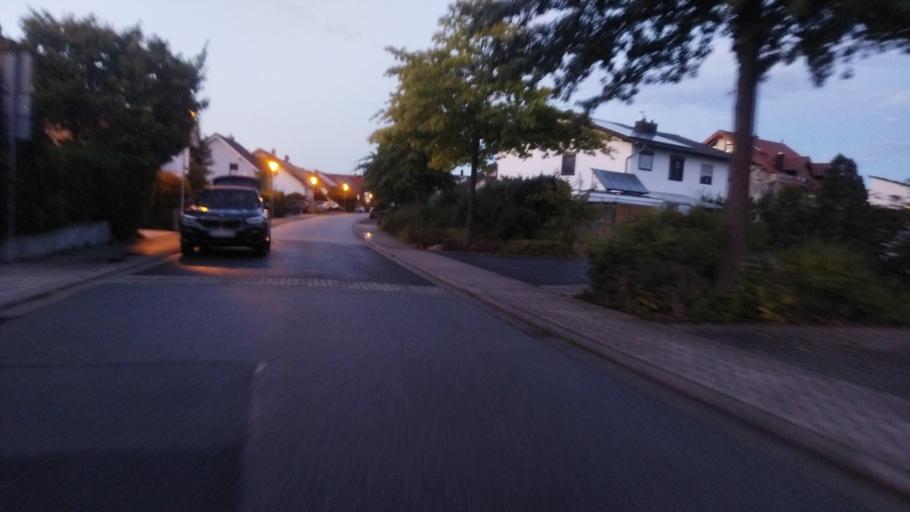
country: DE
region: Hesse
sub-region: Regierungsbezirk Darmstadt
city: Einhausen
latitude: 49.6745
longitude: 8.5368
